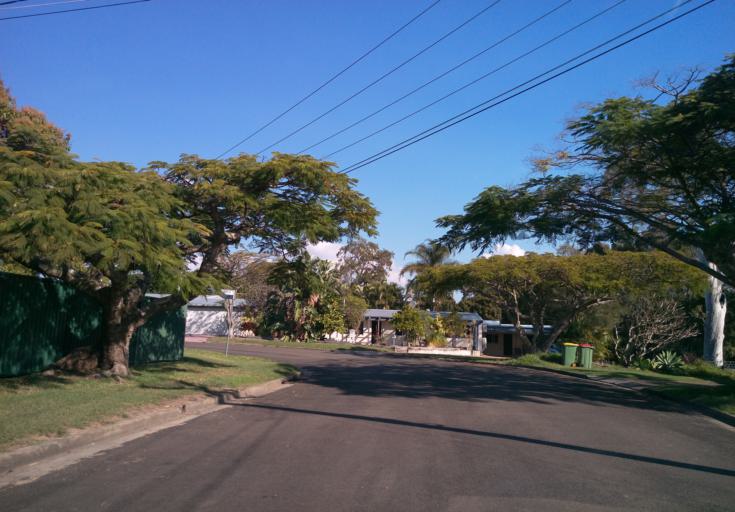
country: AU
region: Queensland
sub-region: Redland
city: Wellington Point
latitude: -27.5117
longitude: 153.2099
